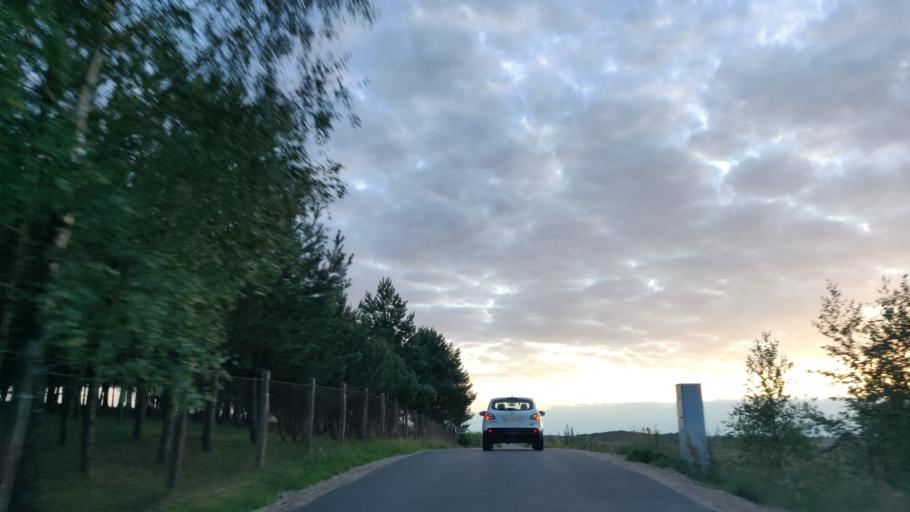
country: LT
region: Vilnius County
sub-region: Trakai
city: Rudiskes
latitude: 54.6083
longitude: 24.8028
